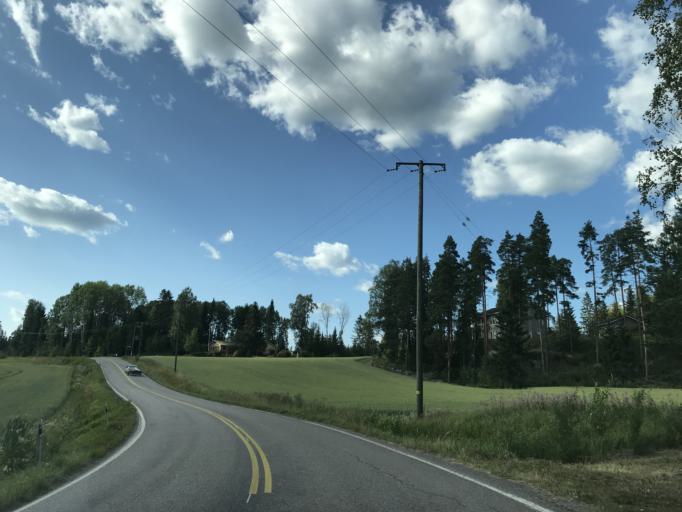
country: FI
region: Uusimaa
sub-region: Helsinki
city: Nurmijaervi
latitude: 60.4486
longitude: 24.6551
